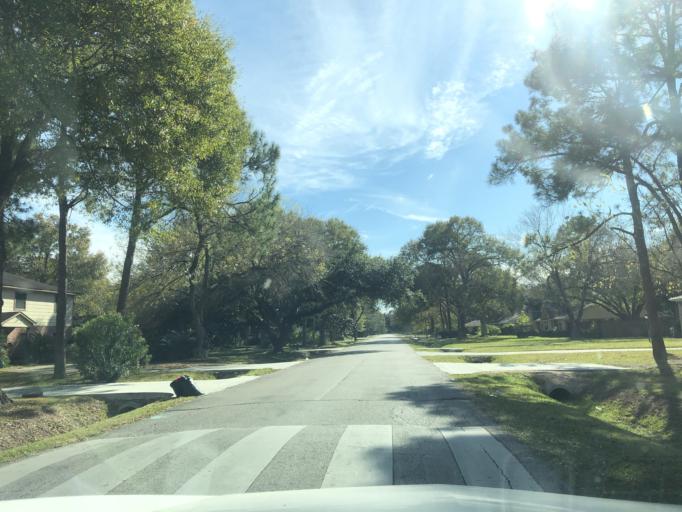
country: US
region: Texas
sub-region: Harris County
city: Bellaire
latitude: 29.6833
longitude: -95.5130
